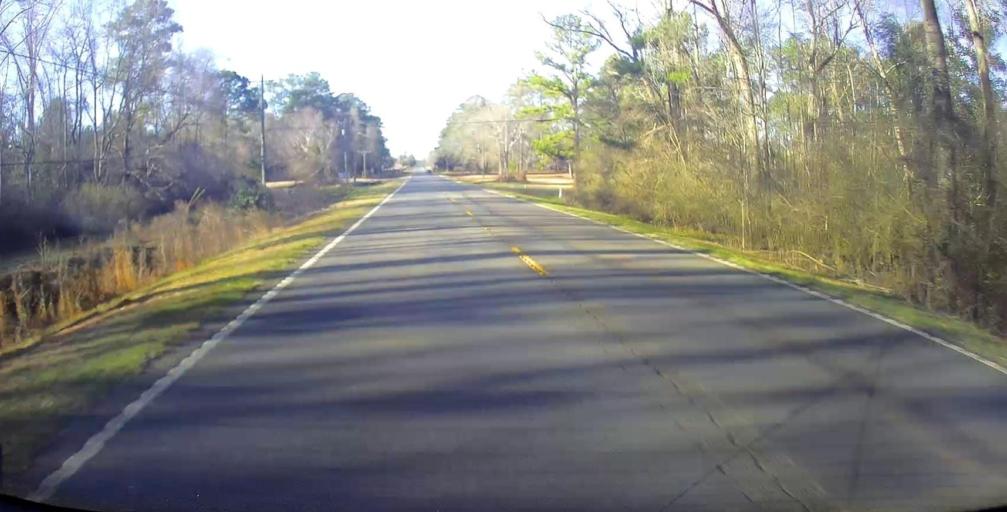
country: US
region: Georgia
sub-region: Sumter County
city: Americus
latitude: 32.0398
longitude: -84.2212
